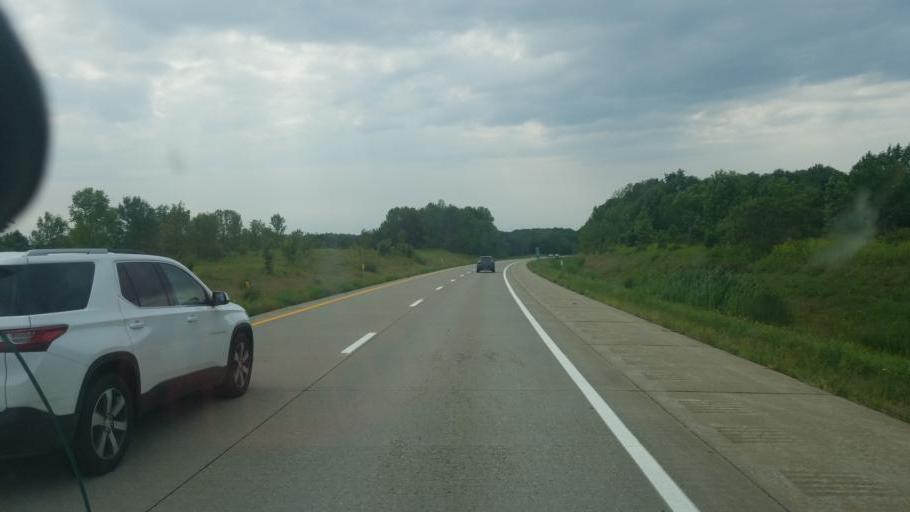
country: US
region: New York
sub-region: Chautauqua County
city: Clymer
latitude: 42.1437
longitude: -79.6761
